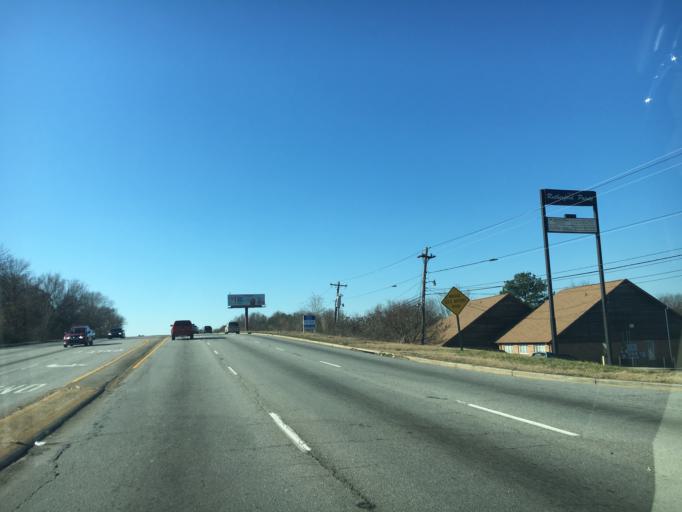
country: US
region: South Carolina
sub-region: Greenville County
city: Wade Hampton
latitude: 34.9148
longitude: -82.3199
